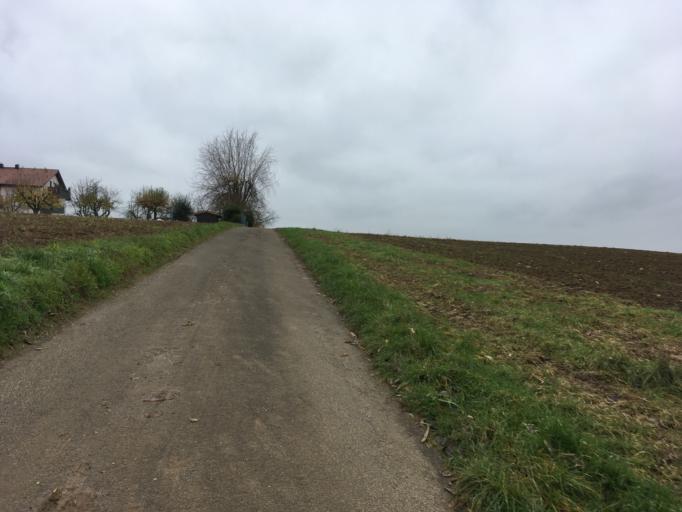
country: DE
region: Baden-Wuerttemberg
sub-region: Regierungsbezirk Stuttgart
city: Heilbronn
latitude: 49.1646
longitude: 9.1932
